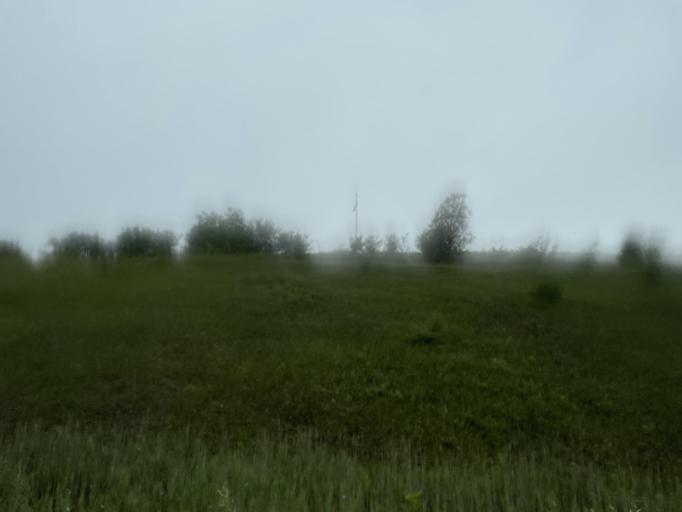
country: CA
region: Ontario
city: Cambridge
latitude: 43.4293
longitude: -80.3302
